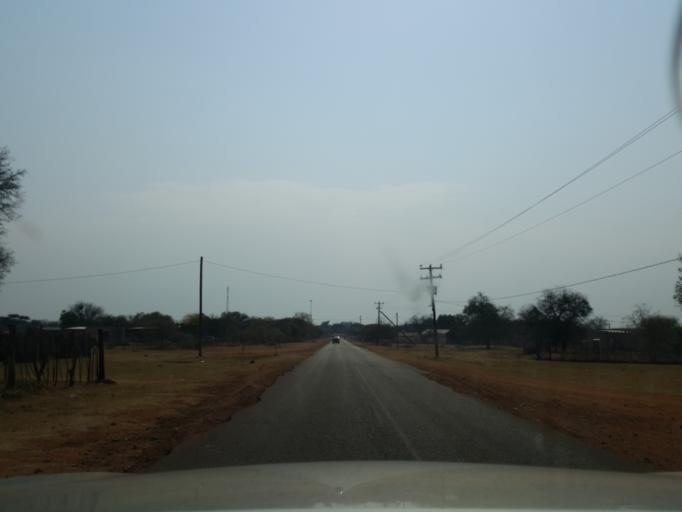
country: BW
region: South East
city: Lobatse
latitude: -25.2884
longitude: 25.9082
